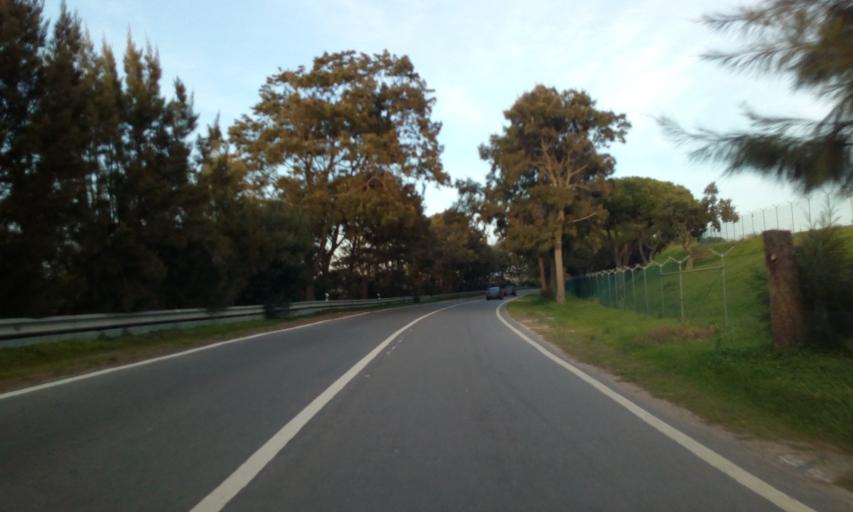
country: PT
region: Faro
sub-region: Faro
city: Faro
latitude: 37.0185
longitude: -7.9877
